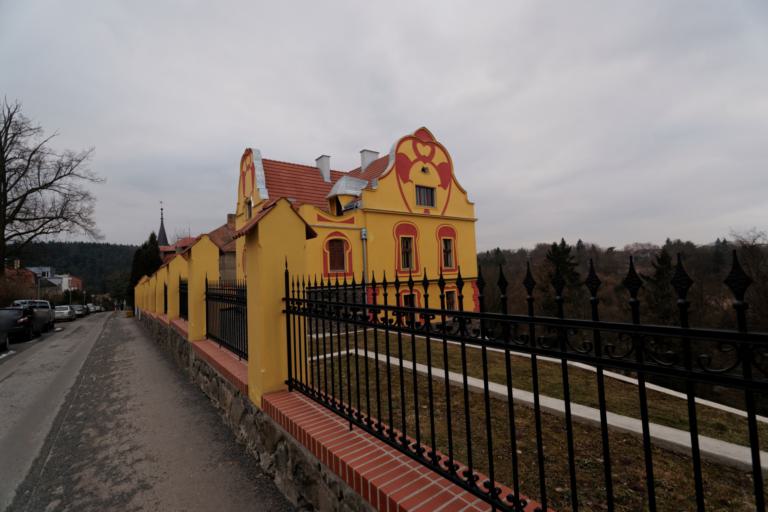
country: CZ
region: Jihocesky
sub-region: Okres Tabor
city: Tabor
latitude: 49.4107
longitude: 14.6543
